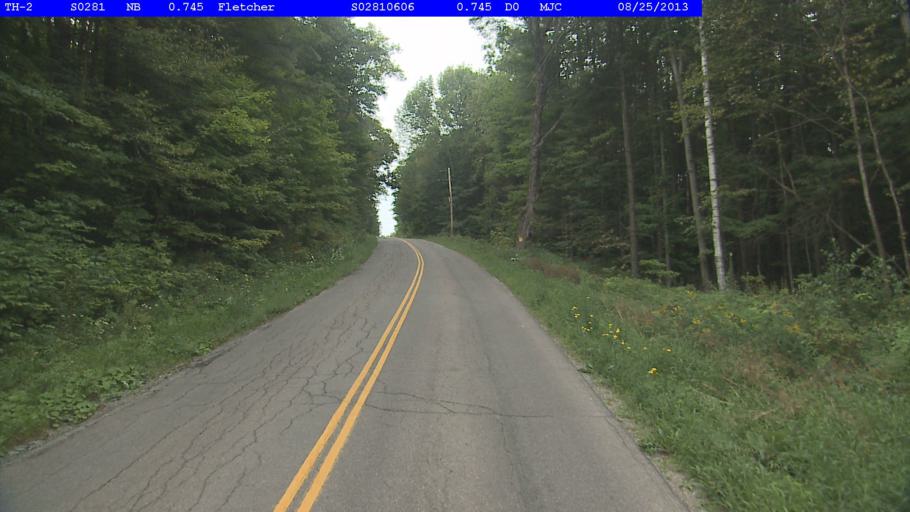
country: US
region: Vermont
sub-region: Chittenden County
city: Milton
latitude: 44.6896
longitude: -72.9257
